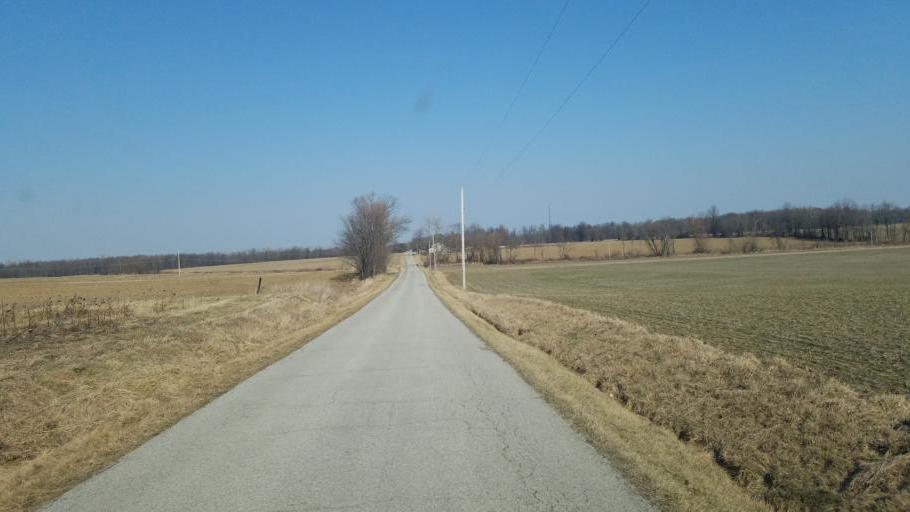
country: US
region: Ohio
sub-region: Crawford County
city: Crestline
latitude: 40.7676
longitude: -82.7652
